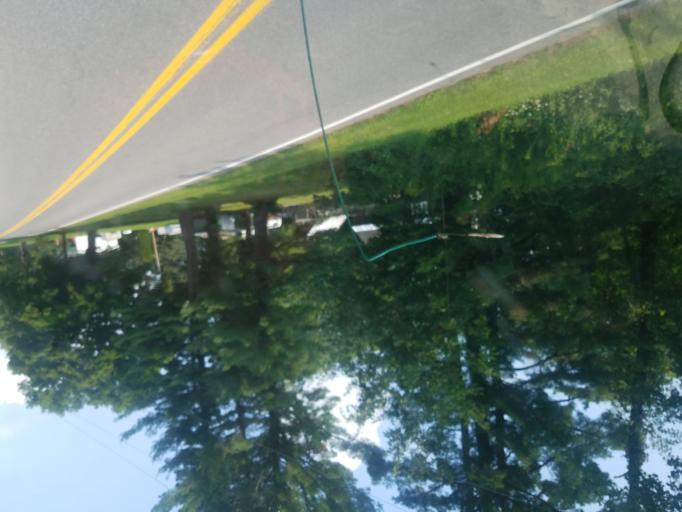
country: US
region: New York
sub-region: Montgomery County
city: Tribes Hill
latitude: 42.9180
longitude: -74.3249
